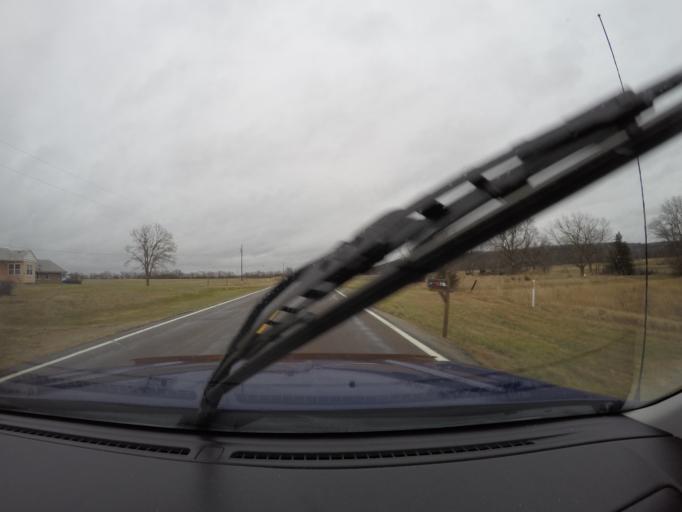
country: US
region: Kansas
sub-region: Jefferson County
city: Valley Falls
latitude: 39.3545
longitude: -95.5267
